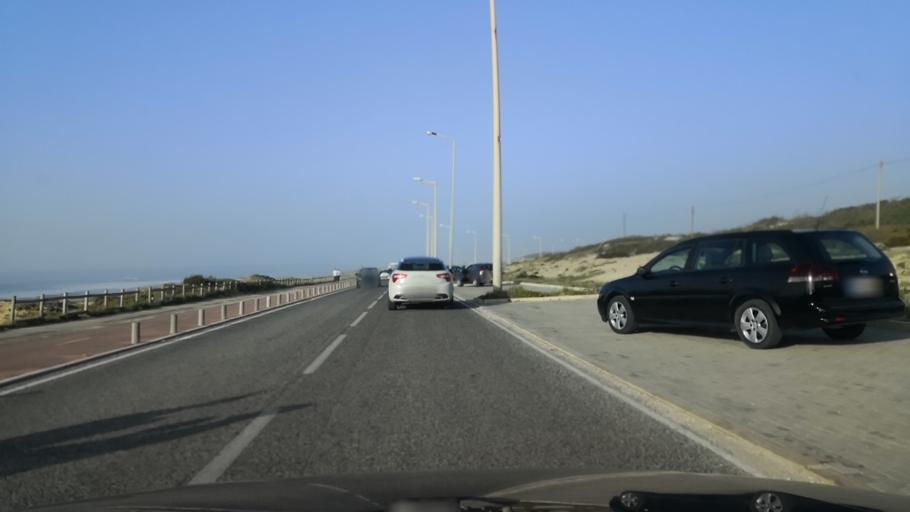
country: PT
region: Leiria
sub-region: Marinha Grande
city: Marinha Grande
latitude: 39.7655
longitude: -9.0303
